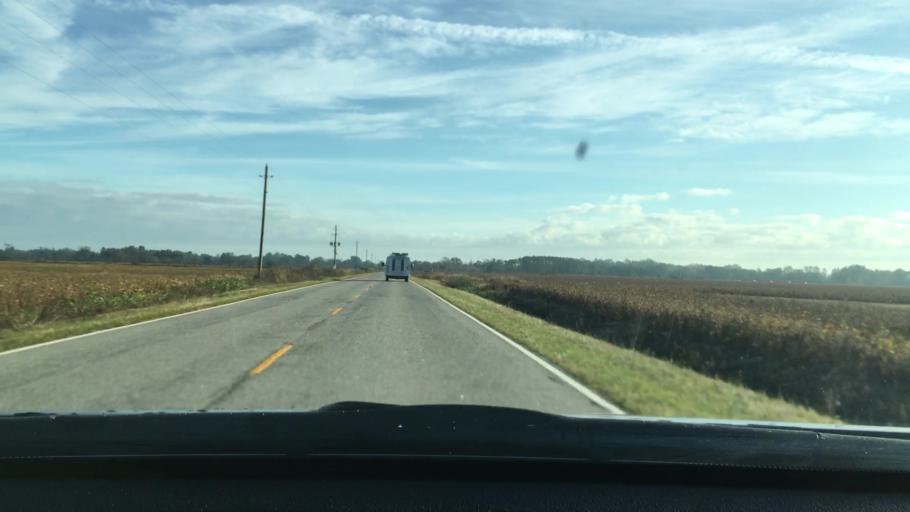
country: US
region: South Carolina
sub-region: Sumter County
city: East Sumter
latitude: 34.0579
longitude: -80.2340
